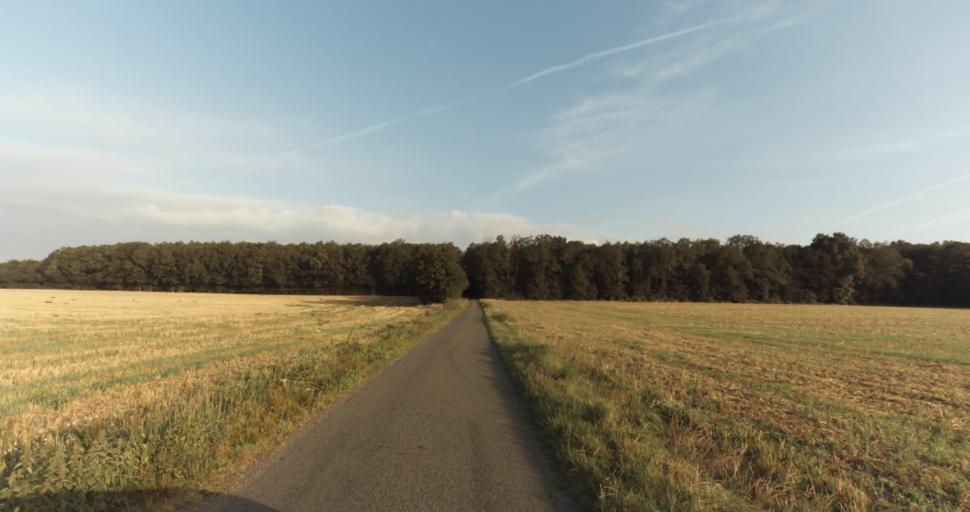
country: FR
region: Centre
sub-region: Departement d'Eure-et-Loir
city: Vert-en-Drouais
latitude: 48.7743
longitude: 1.3230
